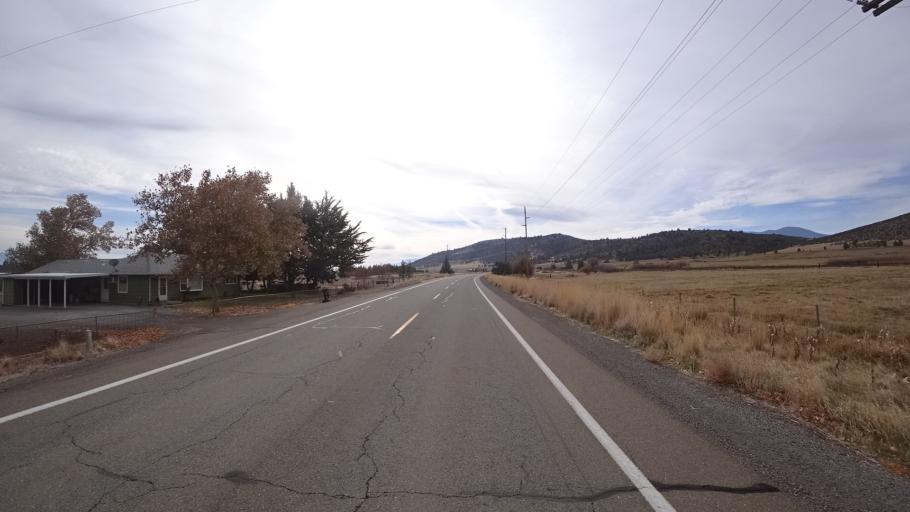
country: US
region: California
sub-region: Siskiyou County
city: Montague
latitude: 41.6915
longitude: -122.5350
